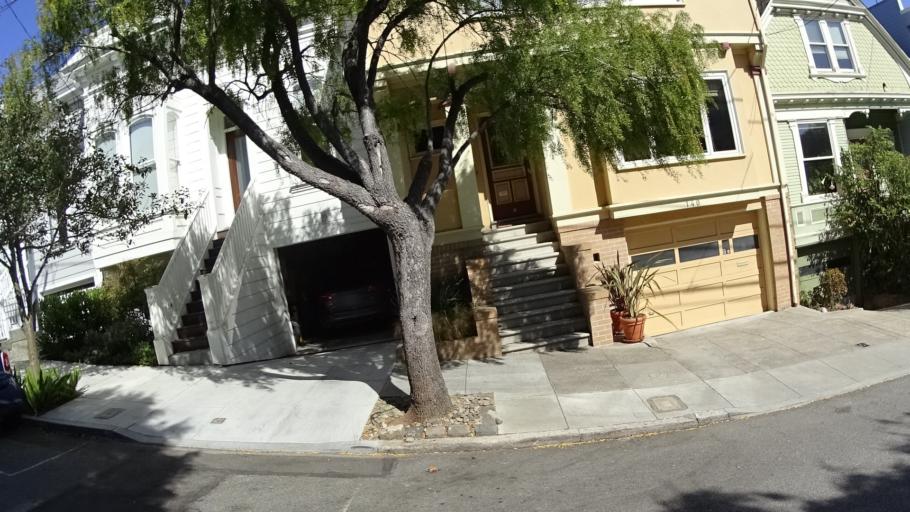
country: US
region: California
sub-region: San Francisco County
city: San Francisco
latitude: 37.7389
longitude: -122.4265
